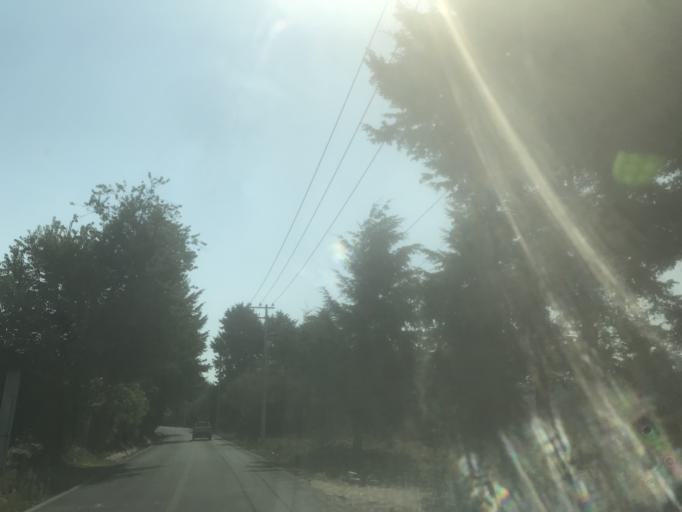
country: MX
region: Mexico
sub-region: Atlautla
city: San Juan Tepecoculco
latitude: 18.9923
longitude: -98.7890
